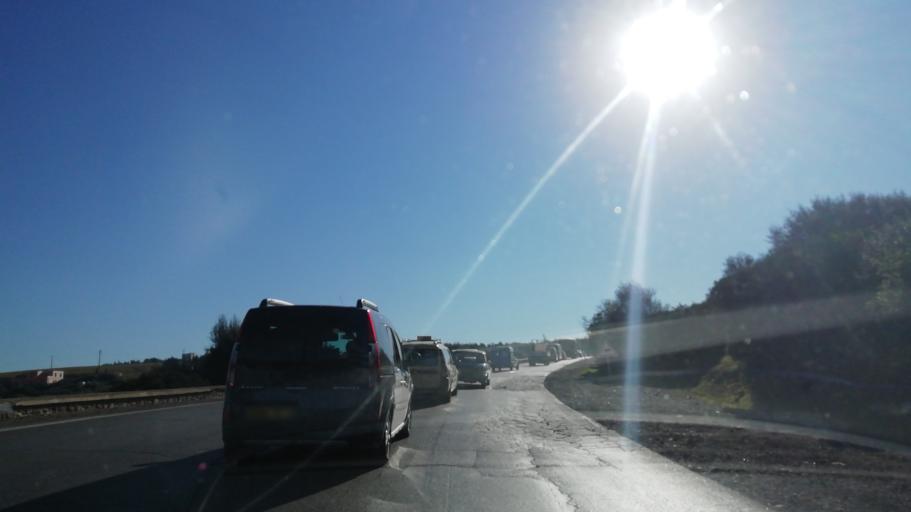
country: DZ
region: Relizane
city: Smala
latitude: 35.6994
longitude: 0.7777
